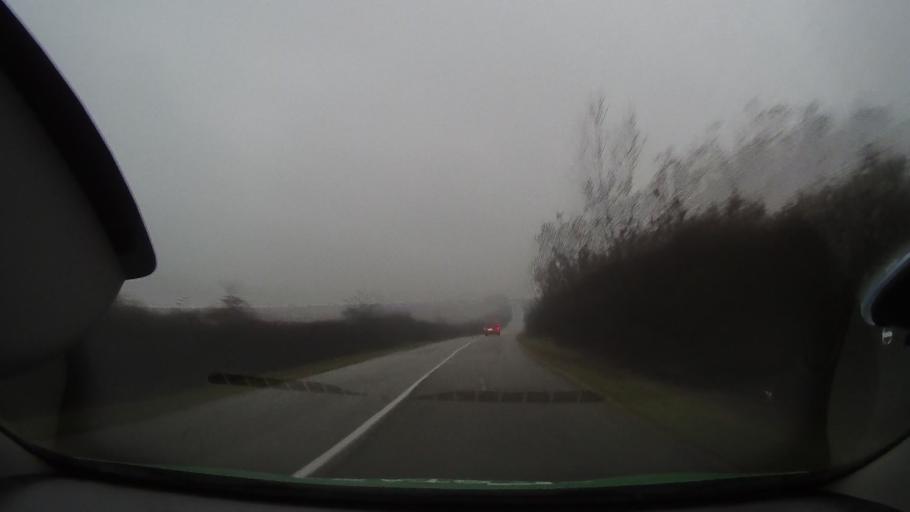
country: RO
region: Arad
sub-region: Comuna Craiova
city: Craiova
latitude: 46.6189
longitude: 21.9583
